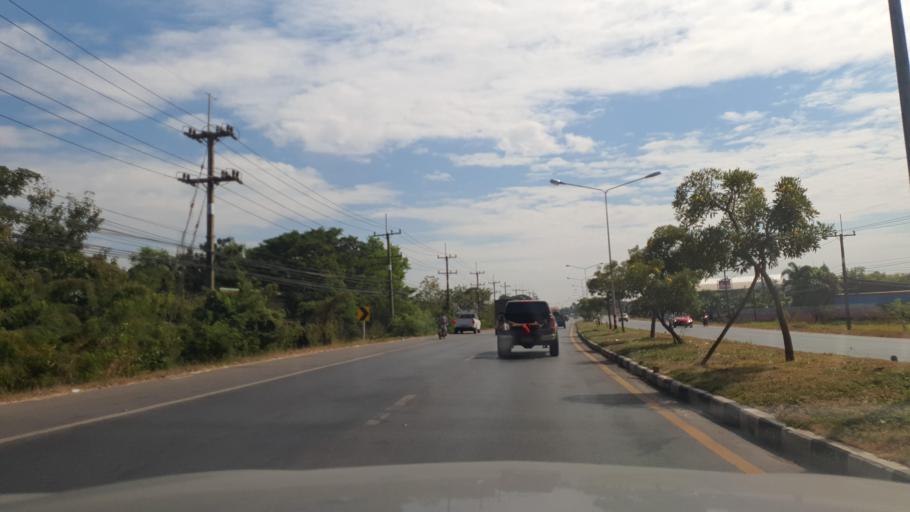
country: TH
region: Kalasin
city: Yang Talat
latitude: 16.4054
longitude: 103.4268
